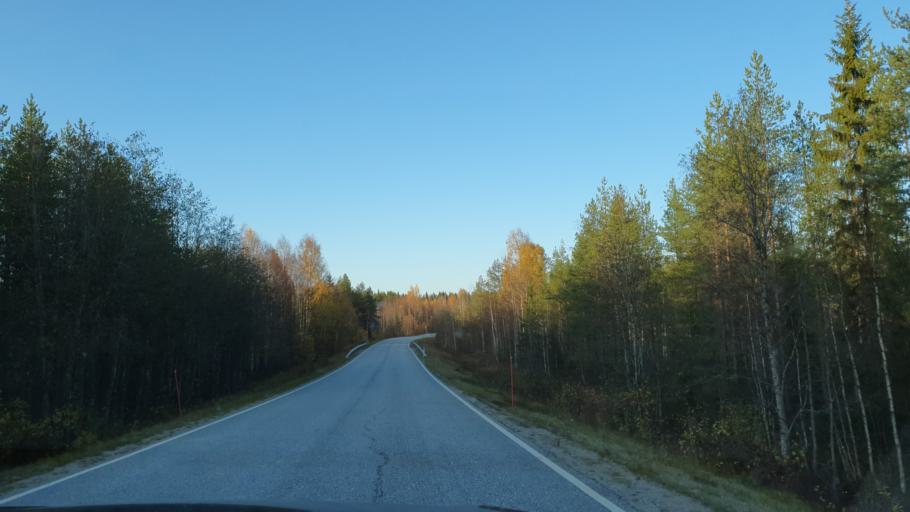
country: FI
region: Kainuu
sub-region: Kehys-Kainuu
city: Kuhmo
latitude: 64.4012
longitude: 29.4679
